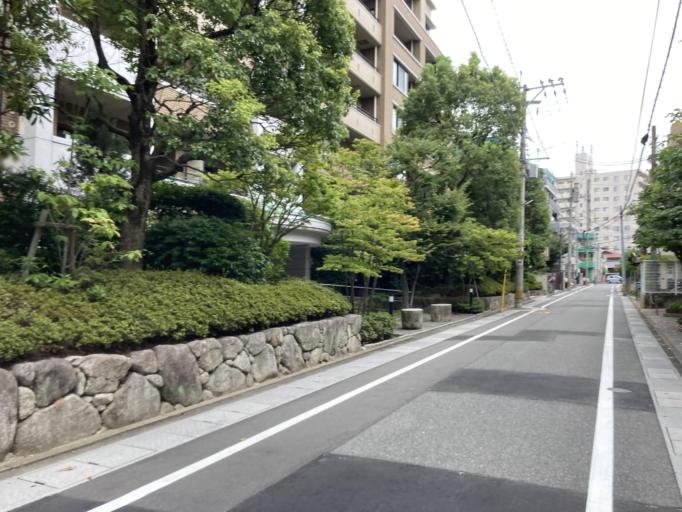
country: JP
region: Fukuoka
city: Fukuoka-shi
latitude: 33.5805
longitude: 130.3474
